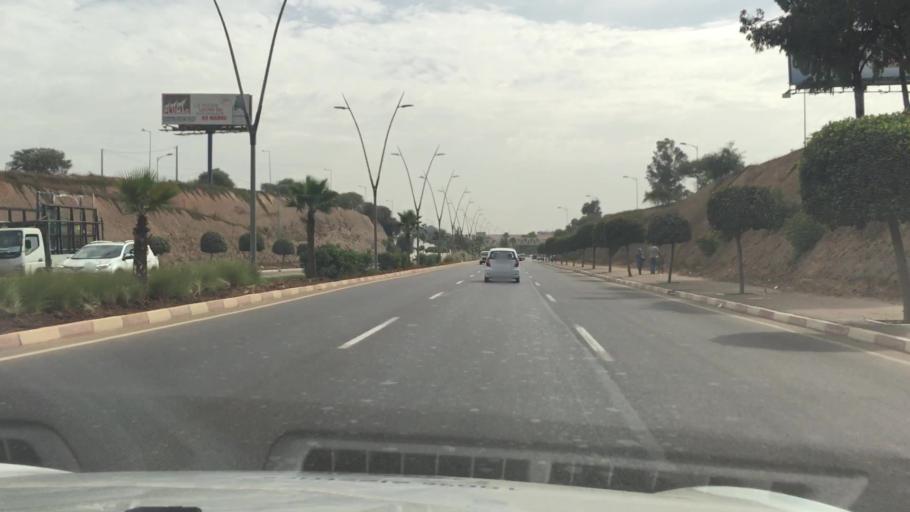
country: MA
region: Grand Casablanca
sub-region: Nouaceur
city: Bouskoura
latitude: 33.5188
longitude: -7.6330
